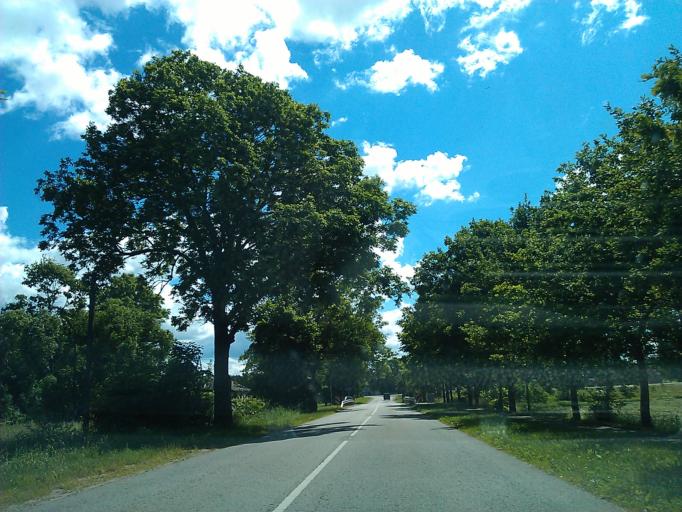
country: LV
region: Varaklani
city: Varaklani
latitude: 56.6056
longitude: 26.7708
